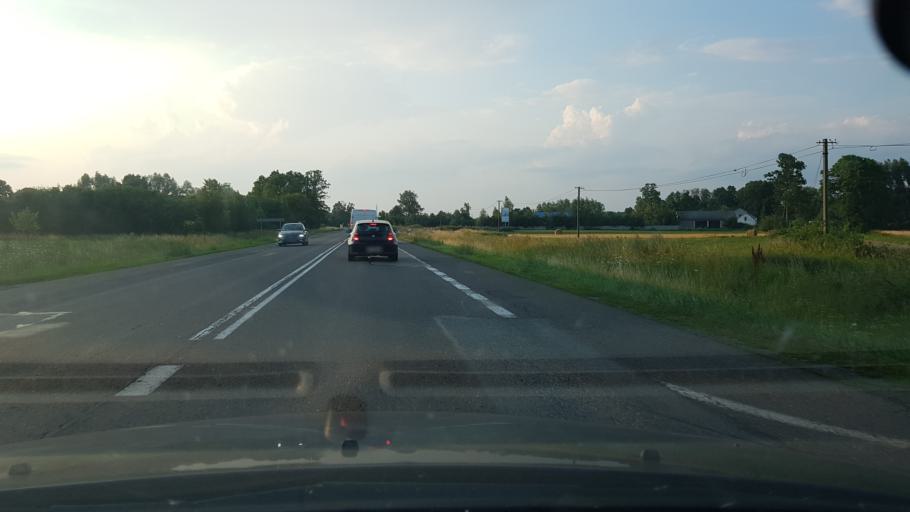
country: PL
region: Masovian Voivodeship
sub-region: Powiat plonski
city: Baboszewo
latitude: 52.7318
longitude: 20.3216
